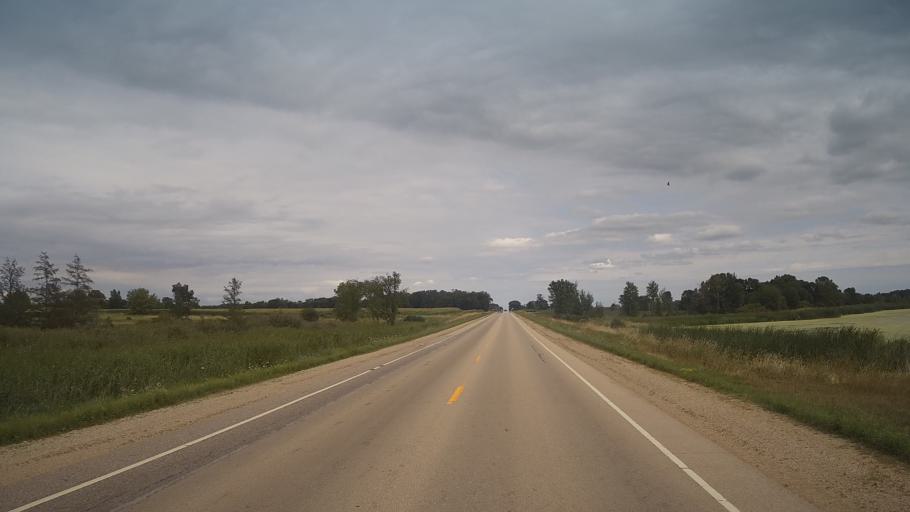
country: US
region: Wisconsin
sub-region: Green Lake County
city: Berlin
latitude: 44.0487
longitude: -88.9521
